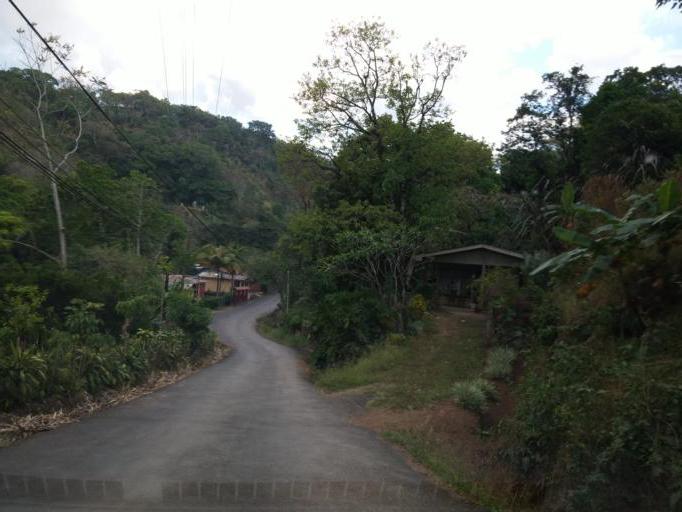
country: CR
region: San Jose
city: Palmichal
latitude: 9.8137
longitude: -84.1904
